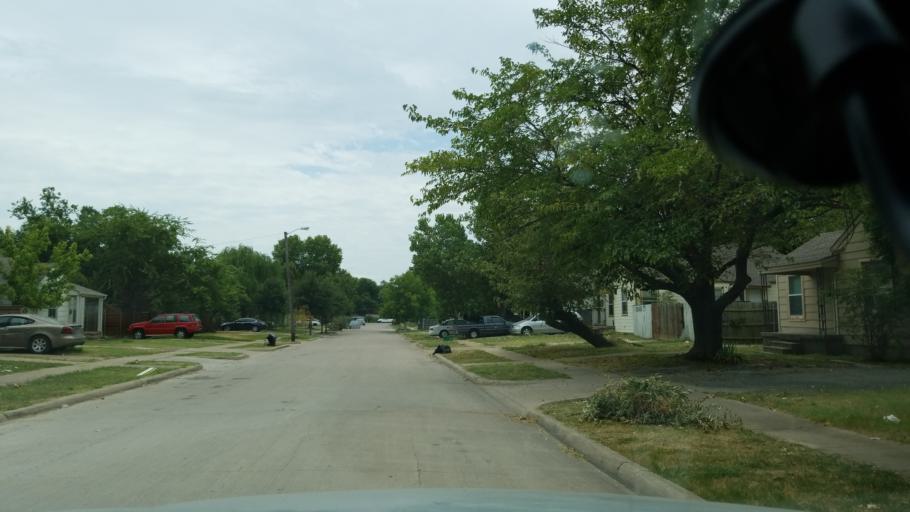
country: US
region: Texas
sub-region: Dallas County
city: Grand Prairie
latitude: 32.7444
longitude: -96.9920
